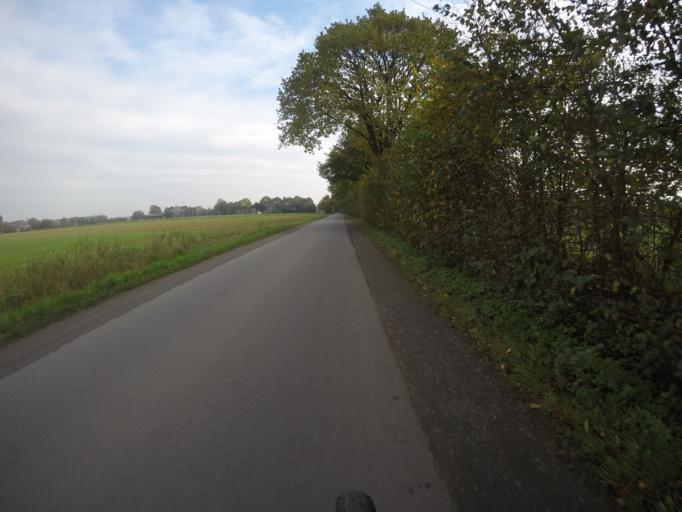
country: DE
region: North Rhine-Westphalia
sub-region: Regierungsbezirk Dusseldorf
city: Bocholt
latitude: 51.8358
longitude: 6.5499
